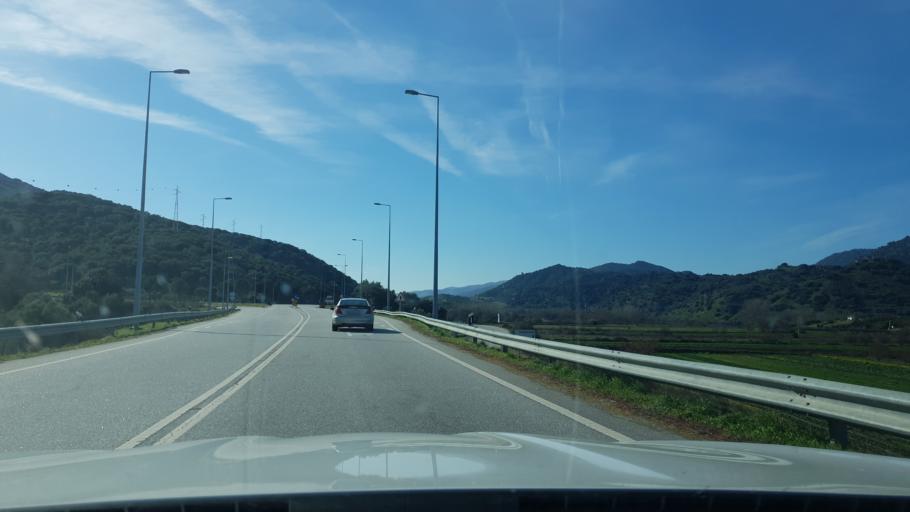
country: PT
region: Braganca
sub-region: Torre de Moncorvo
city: Torre de Moncorvo
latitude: 41.1828
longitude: -7.1026
